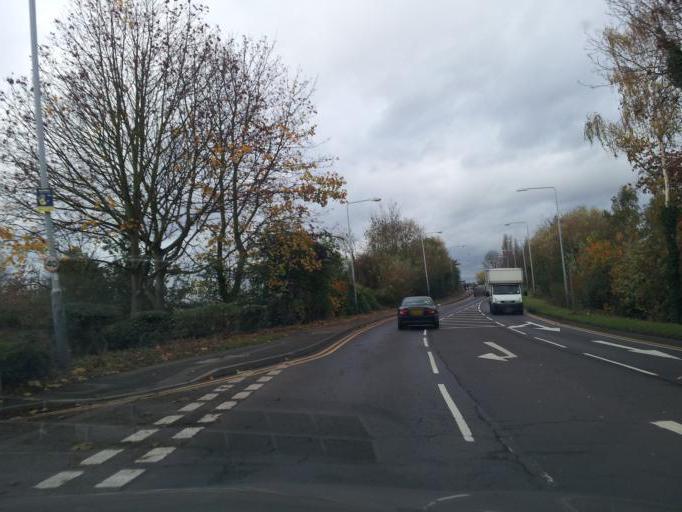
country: GB
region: England
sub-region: Nottinghamshire
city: West Bridgford
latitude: 52.9398
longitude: -1.1295
